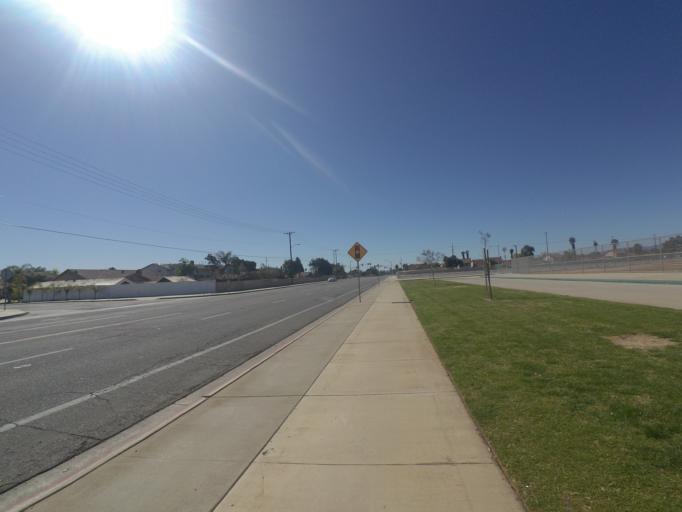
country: US
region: California
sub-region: Riverside County
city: Moreno Valley
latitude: 33.9262
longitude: -117.2526
